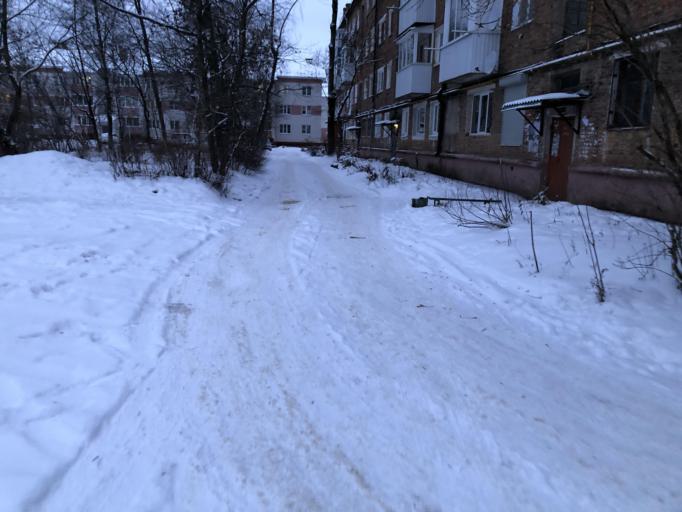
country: RU
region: Smolensk
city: Safonovo
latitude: 55.1141
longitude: 33.2289
